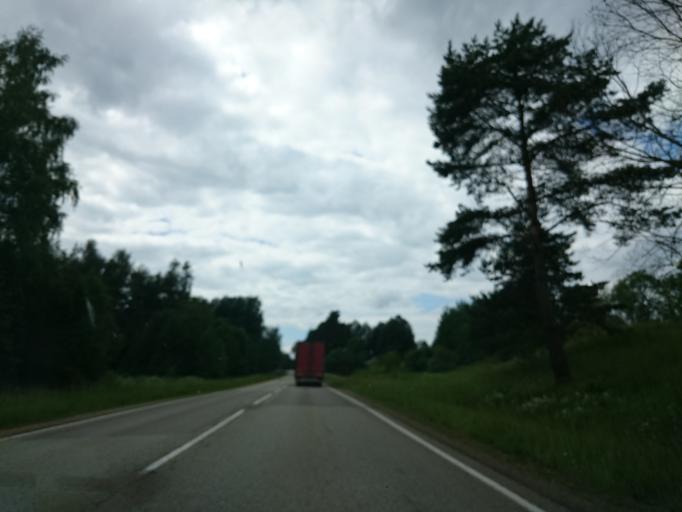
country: LV
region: Ludzas Rajons
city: Ludza
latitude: 56.5342
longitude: 27.5938
